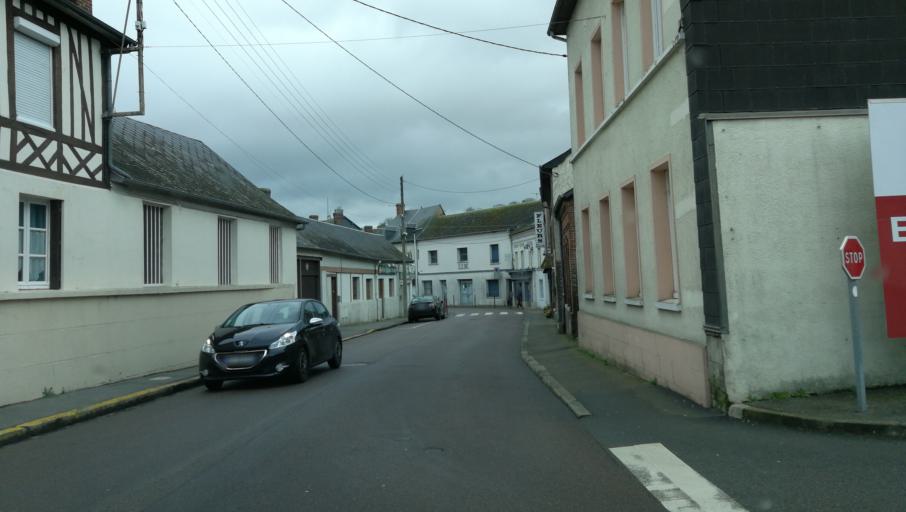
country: FR
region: Haute-Normandie
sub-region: Departement de l'Eure
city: Brionne
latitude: 49.1954
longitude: 0.7164
